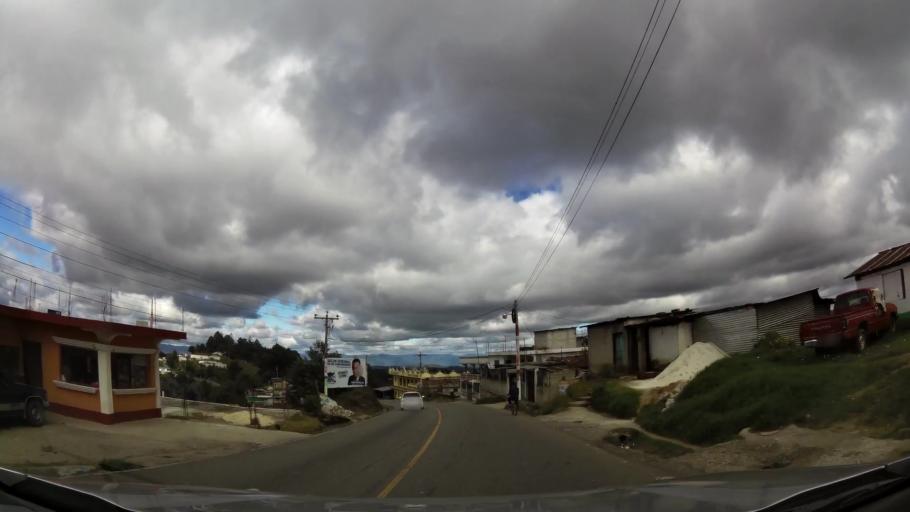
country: GT
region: Quiche
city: Chichicastenango
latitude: 14.8851
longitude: -91.1224
